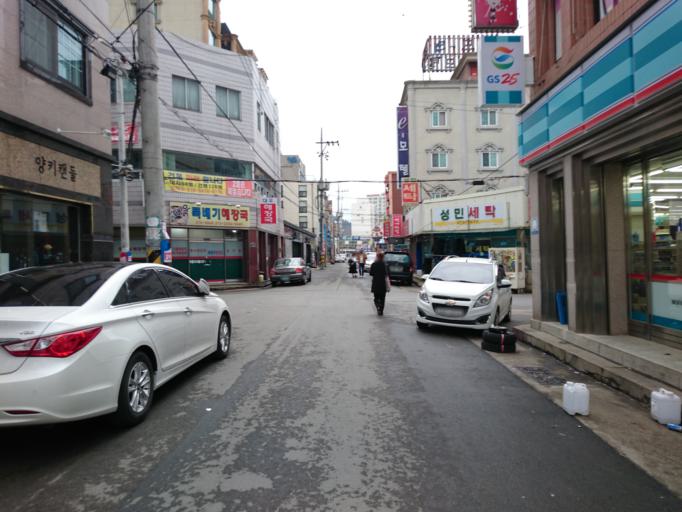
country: KR
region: Gyeongsangbuk-do
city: Enjitsu
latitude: 36.0147
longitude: 129.3472
